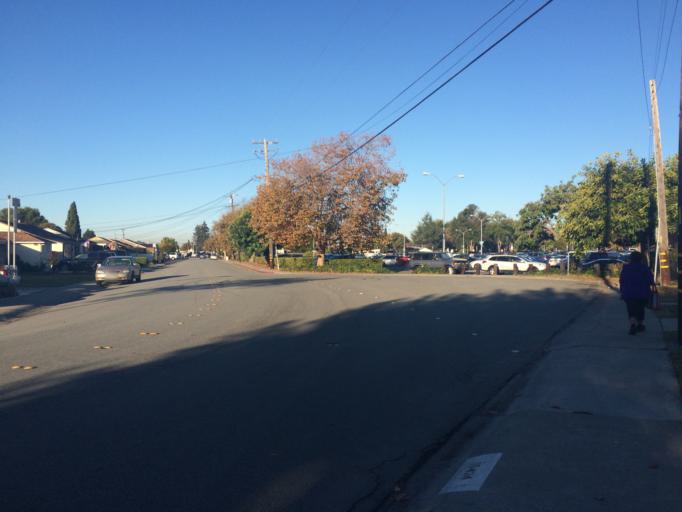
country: US
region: California
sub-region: Alameda County
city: Ashland
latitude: 37.6961
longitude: -122.1264
